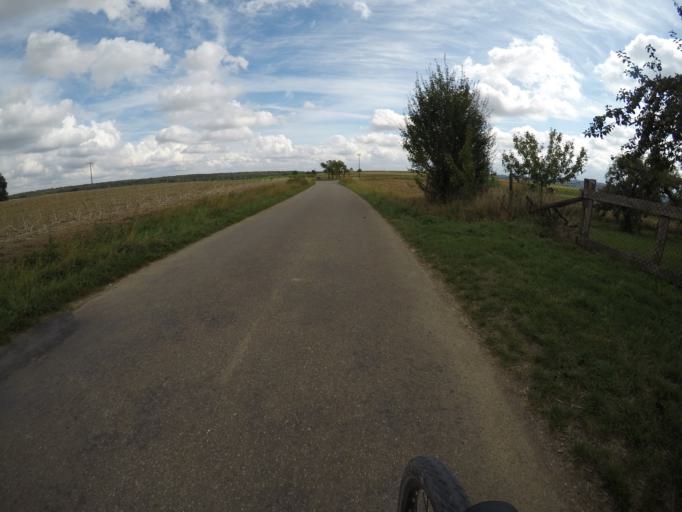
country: DE
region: Baden-Wuerttemberg
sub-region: Regierungsbezirk Stuttgart
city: Deckenpfronn
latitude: 48.6250
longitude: 8.8416
